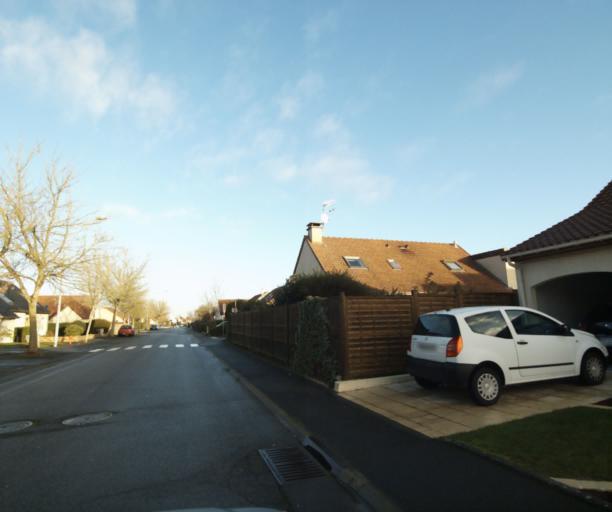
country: FR
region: Pays de la Loire
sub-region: Departement de la Sarthe
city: Sarge-les-le-Mans
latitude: 48.0138
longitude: 0.2312
